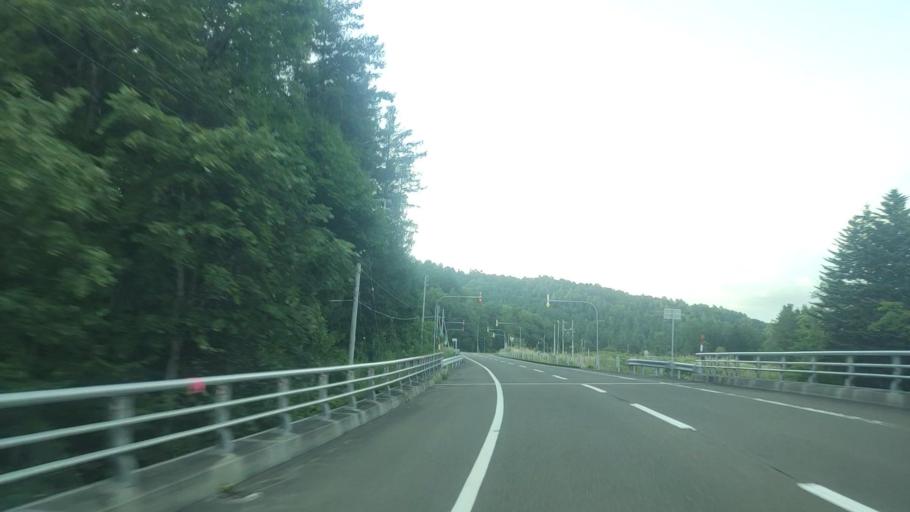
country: JP
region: Hokkaido
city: Bibai
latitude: 43.0610
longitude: 142.0996
